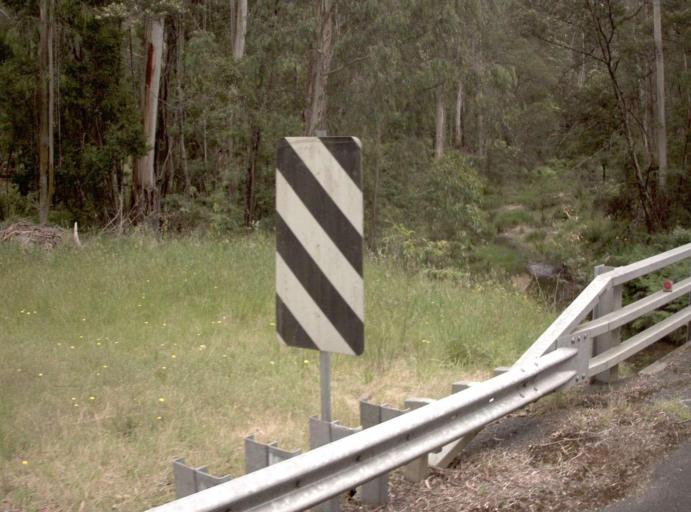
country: AU
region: New South Wales
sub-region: Bombala
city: Bombala
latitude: -37.2834
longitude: 149.2221
